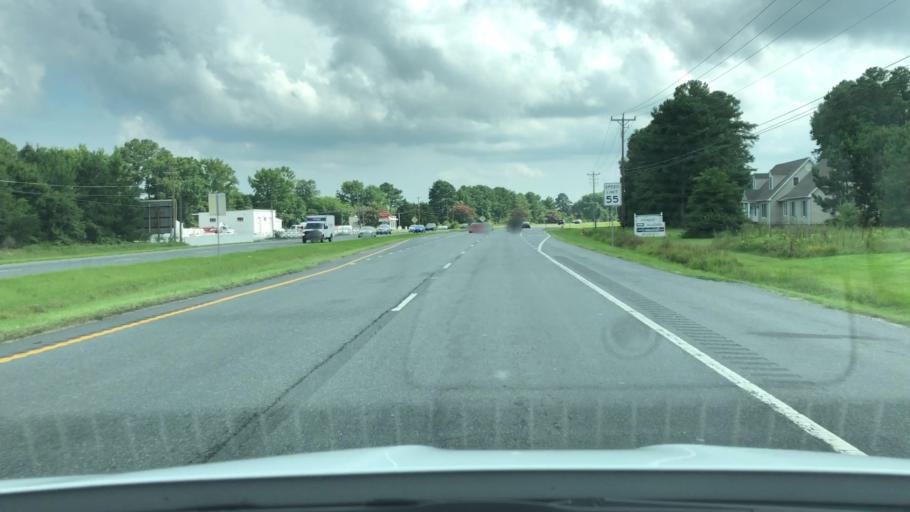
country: US
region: Virginia
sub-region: Accomack County
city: Onancock
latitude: 37.6821
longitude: -75.7229
